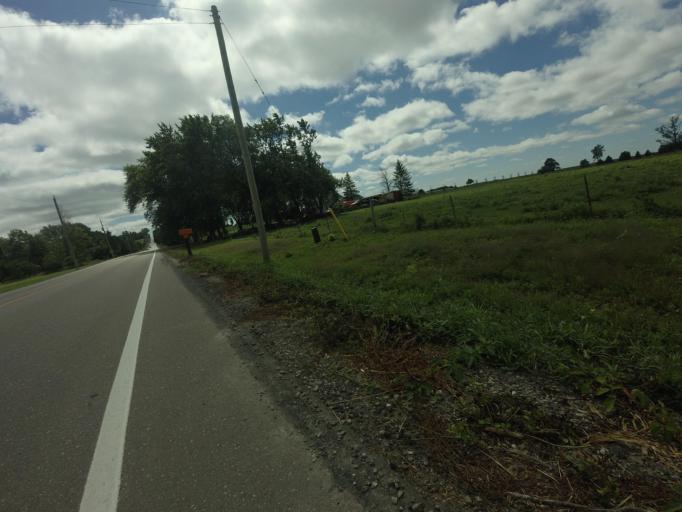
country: CA
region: Ontario
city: Uxbridge
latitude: 44.1259
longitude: -79.1545
